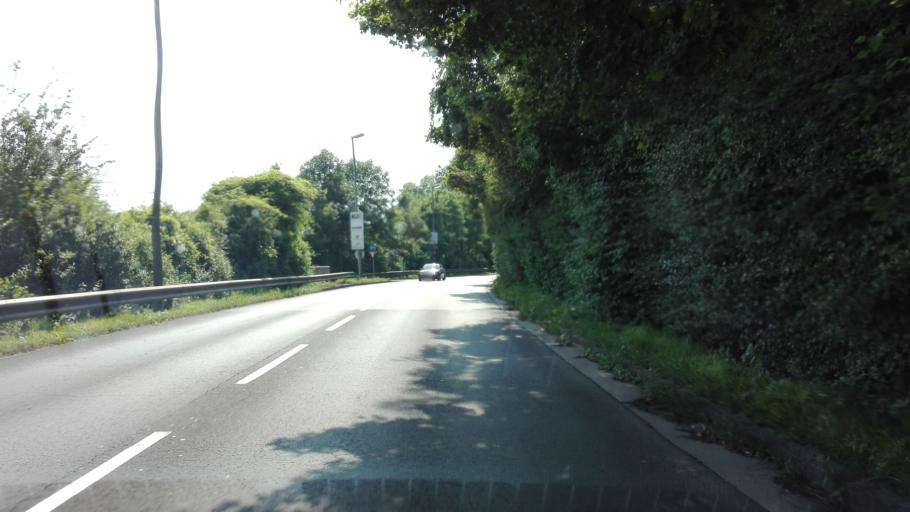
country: AT
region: Upper Austria
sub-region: Politischer Bezirk Linz-Land
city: Ansfelden
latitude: 48.2415
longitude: 14.2956
